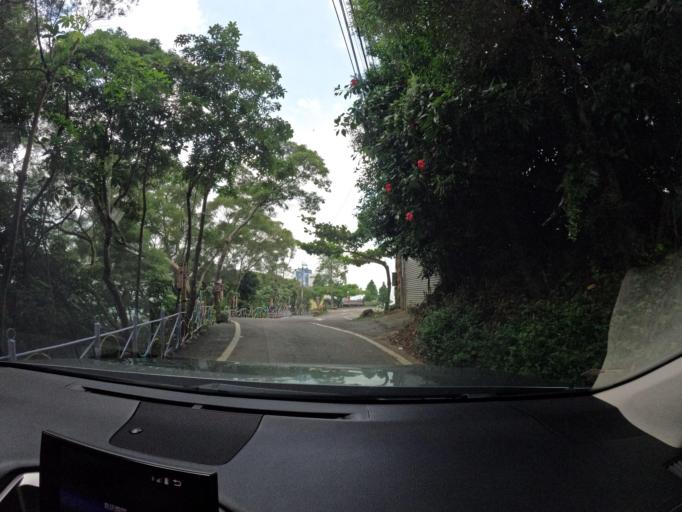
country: TW
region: Taiwan
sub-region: Nantou
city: Nantou
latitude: 23.9105
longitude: 120.6314
